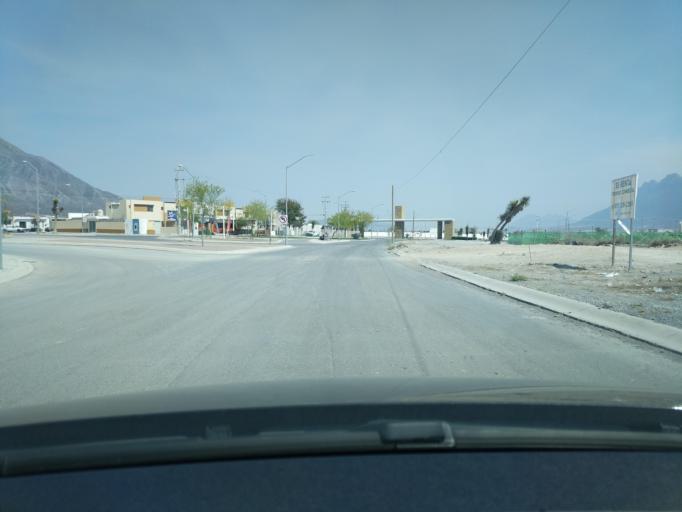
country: MX
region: Nuevo Leon
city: Garcia
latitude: 25.8146
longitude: -100.5397
